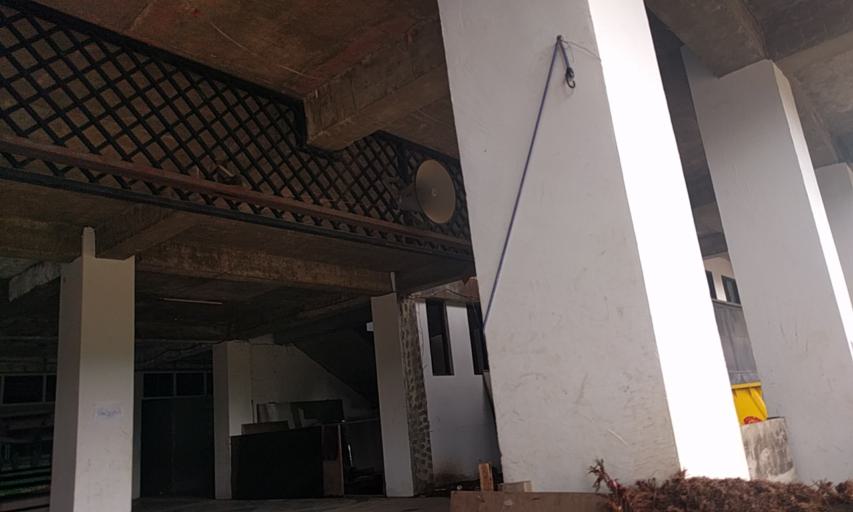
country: MM
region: Mon
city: Mawlamyine
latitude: 16.4549
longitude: 97.6477
